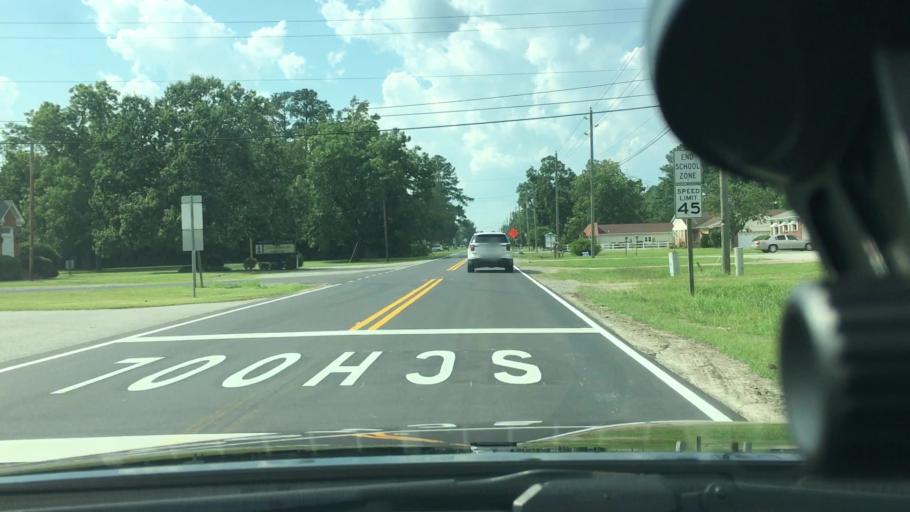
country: US
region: North Carolina
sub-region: Craven County
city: James City
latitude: 35.0693
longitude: -77.0199
